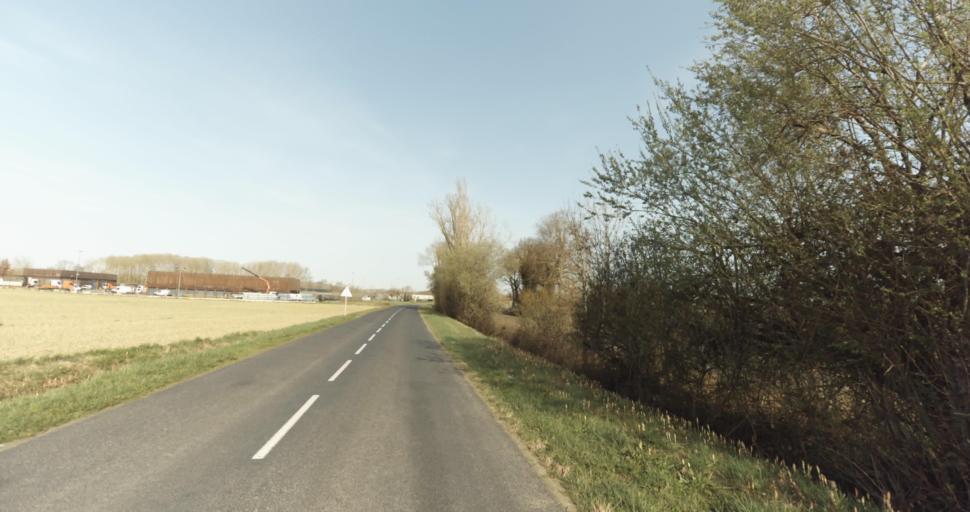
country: FR
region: Midi-Pyrenees
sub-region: Departement du Tarn
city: Saint-Sulpice-la-Pointe
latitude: 43.7660
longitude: 1.7194
